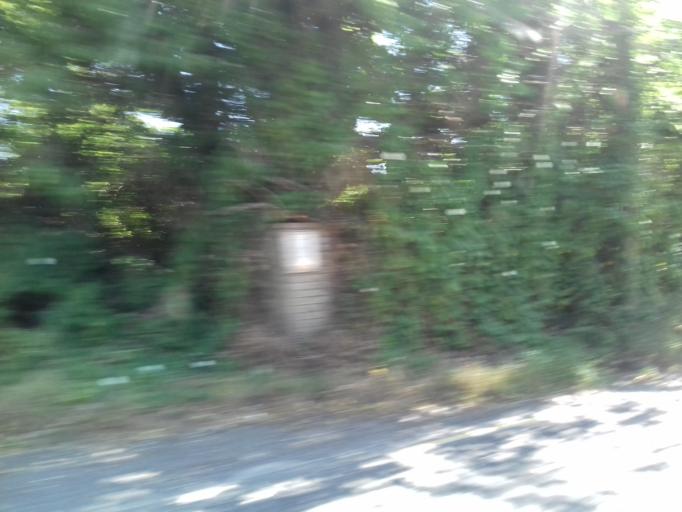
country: IE
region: Leinster
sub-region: Fingal County
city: Swords
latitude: 53.4591
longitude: -6.2677
